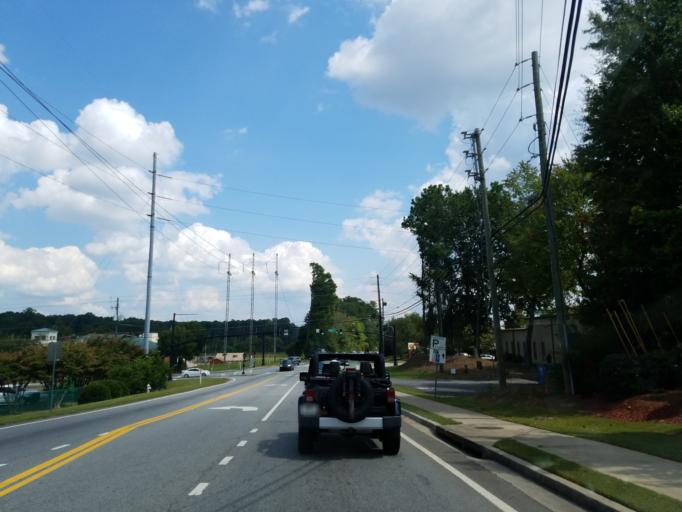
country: US
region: Georgia
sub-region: Fulton County
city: Alpharetta
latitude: 34.0608
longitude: -84.3036
